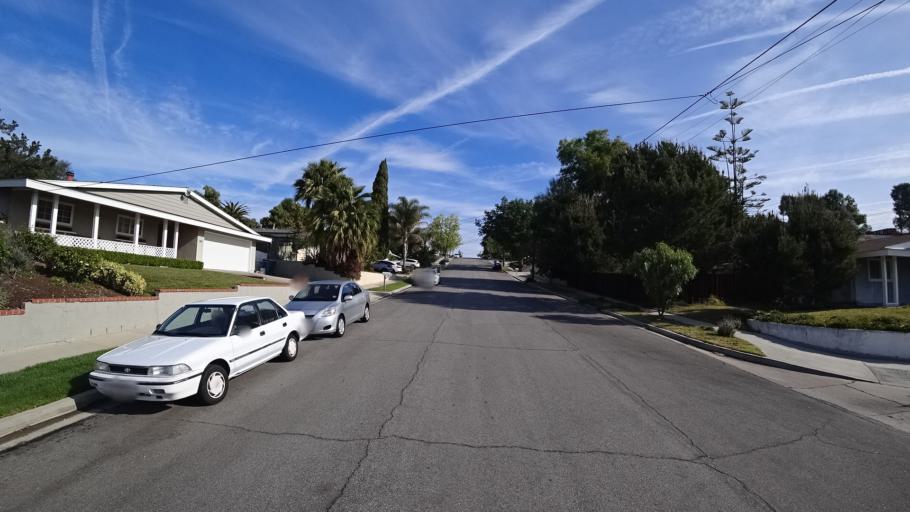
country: US
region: California
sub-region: Ventura County
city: Thousand Oaks
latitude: 34.1888
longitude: -118.8739
